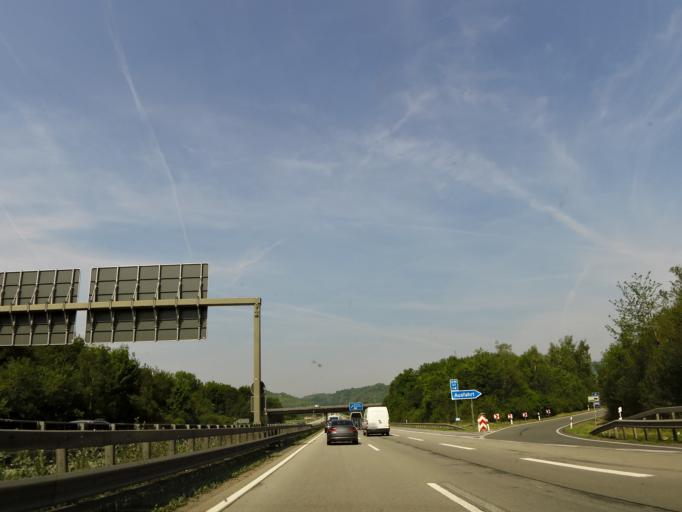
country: DE
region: Rheinland-Pfalz
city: Laubenheim
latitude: 49.9320
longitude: 7.9185
